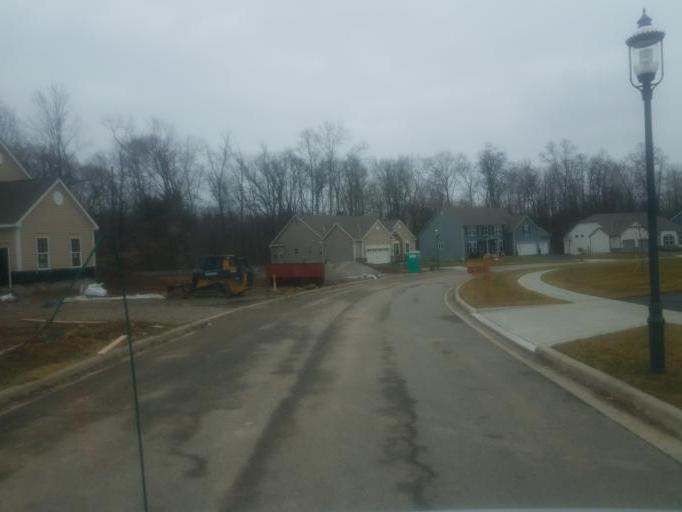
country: US
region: Ohio
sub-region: Delaware County
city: Sunbury
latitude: 40.2206
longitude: -82.8914
